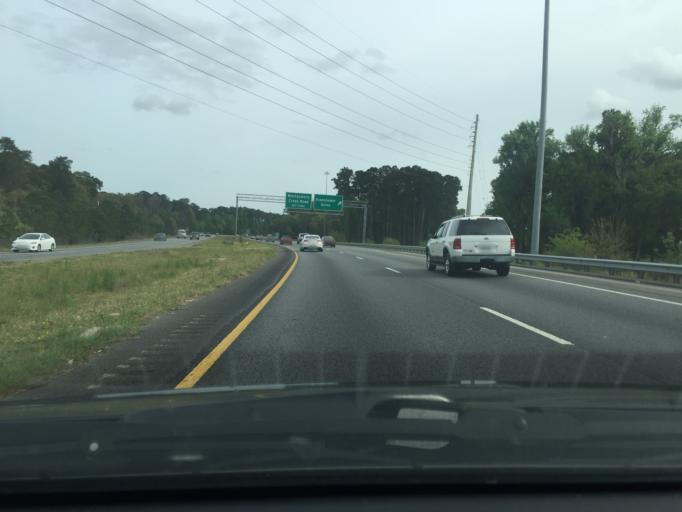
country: US
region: Georgia
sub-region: Chatham County
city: Isle of Hope
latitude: 32.0103
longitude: -81.0820
